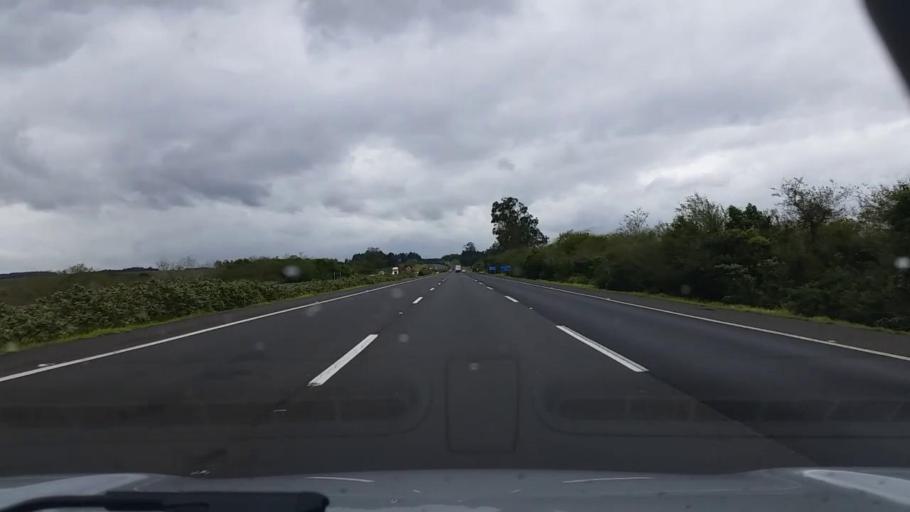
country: BR
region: Rio Grande do Sul
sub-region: Gravatai
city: Gravatai
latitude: -29.9214
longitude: -50.8418
